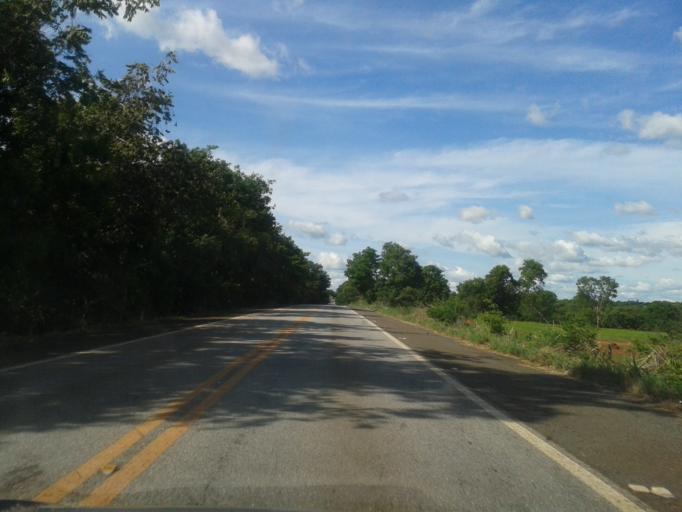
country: BR
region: Goias
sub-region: Mozarlandia
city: Mozarlandia
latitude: -14.9519
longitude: -50.5787
